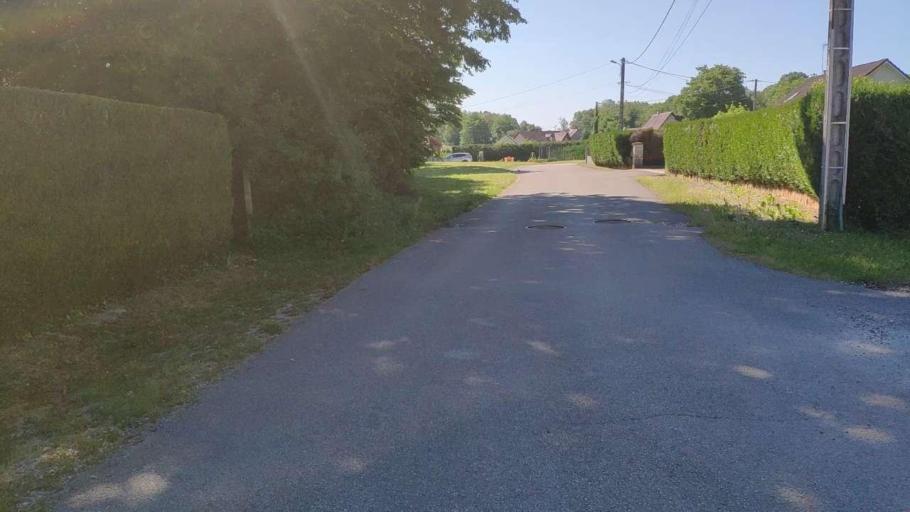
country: FR
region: Franche-Comte
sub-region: Departement du Jura
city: Bletterans
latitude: 46.7999
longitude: 5.4453
